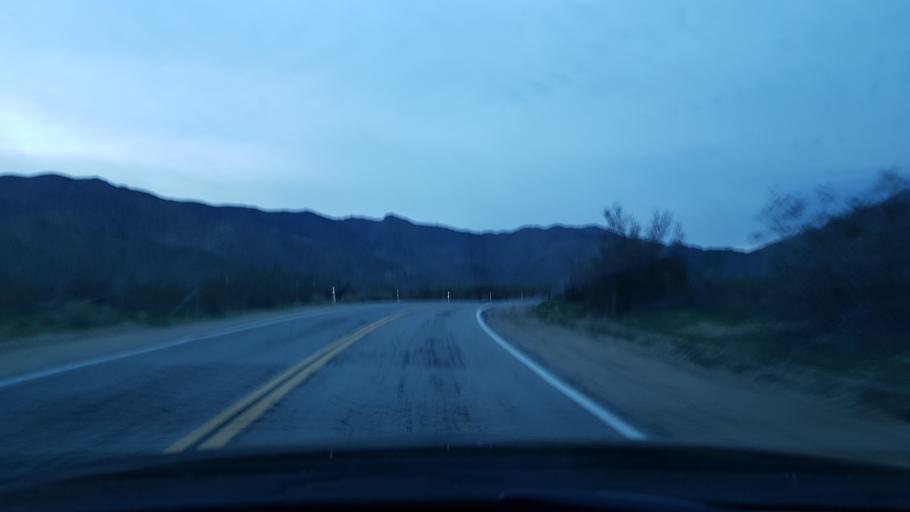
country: US
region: California
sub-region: San Diego County
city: Pine Valley
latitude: 32.9804
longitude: -116.4389
